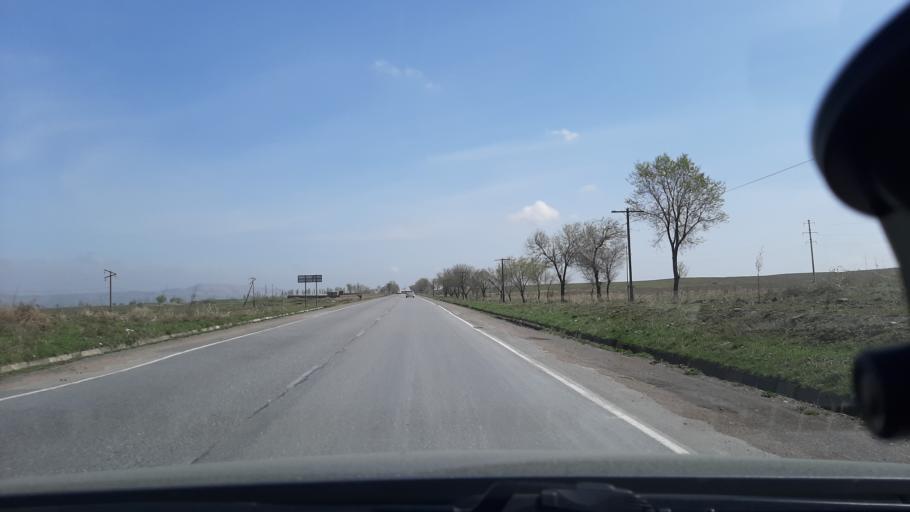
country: TJ
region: Viloyati Sughd
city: Shahriston
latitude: 39.7881
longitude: 68.8676
